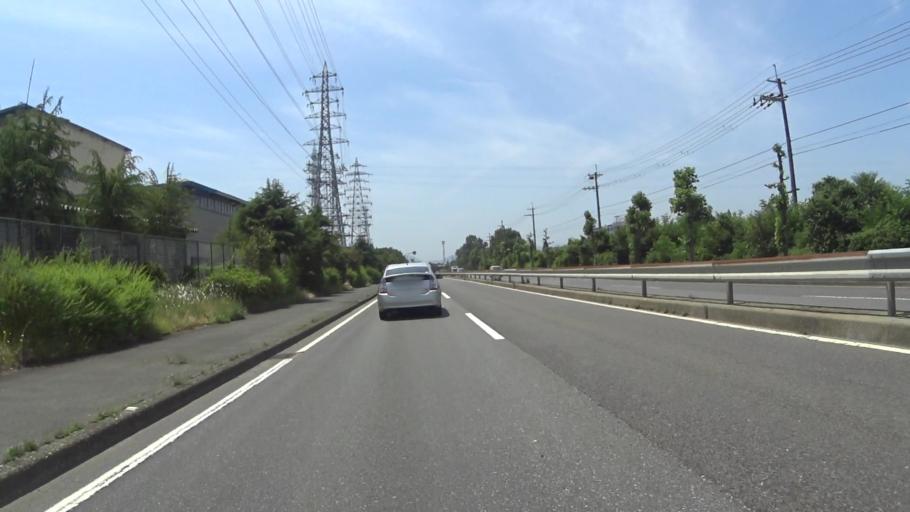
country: JP
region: Kyoto
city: Fukuchiyama
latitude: 35.2861
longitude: 135.1635
